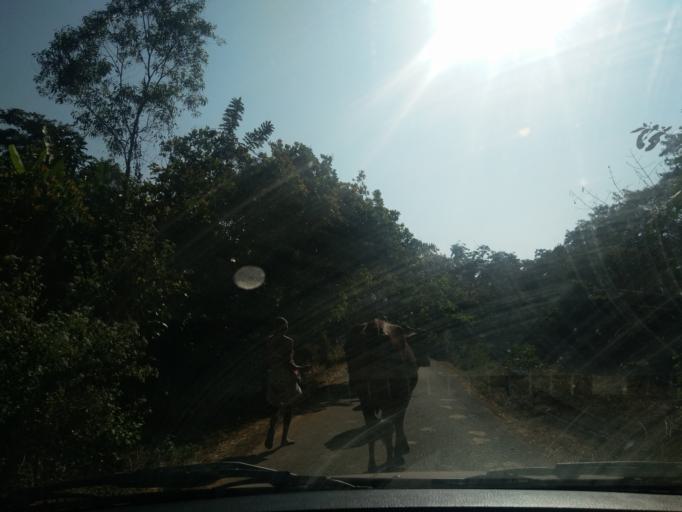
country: IN
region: Goa
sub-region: South Goa
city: Quepem
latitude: 15.1665
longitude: 74.0703
